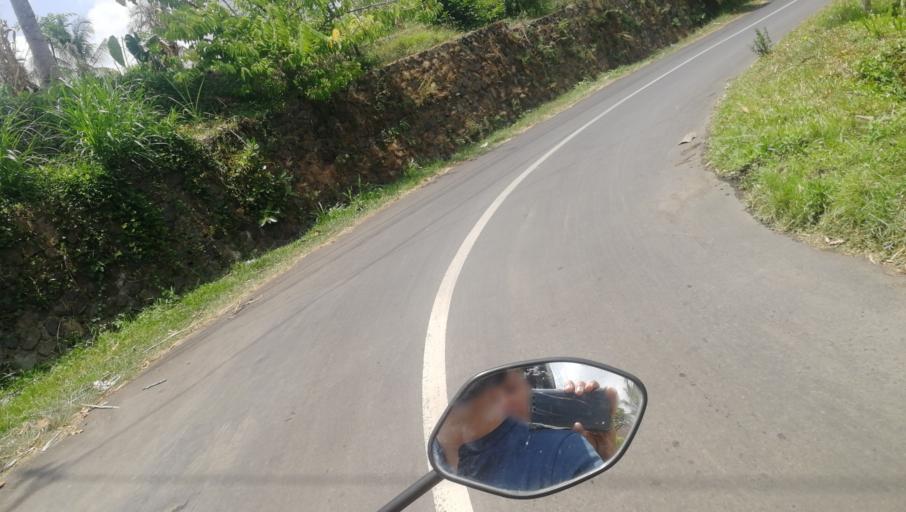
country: ID
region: Bali
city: Banjar Pedawa
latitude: -8.2639
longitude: 115.0303
